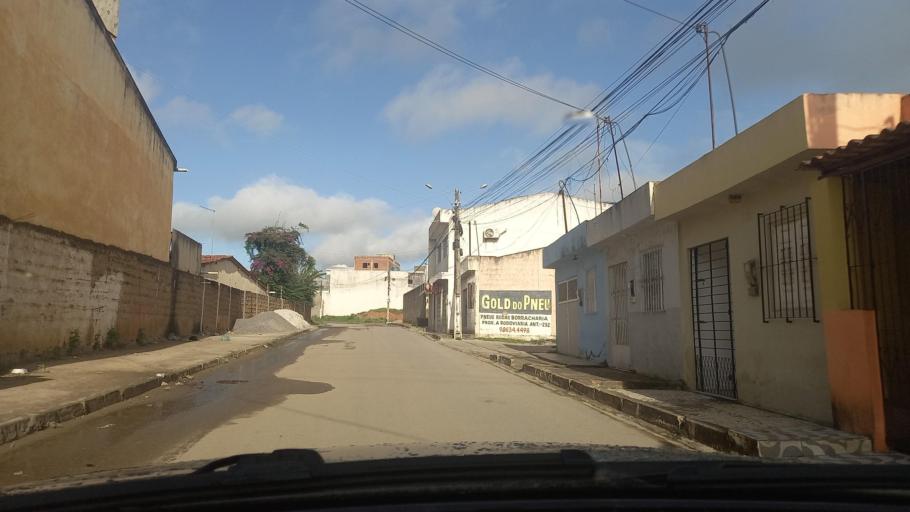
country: BR
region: Pernambuco
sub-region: Vitoria De Santo Antao
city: Vitoria de Santo Antao
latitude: -8.1071
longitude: -35.3048
